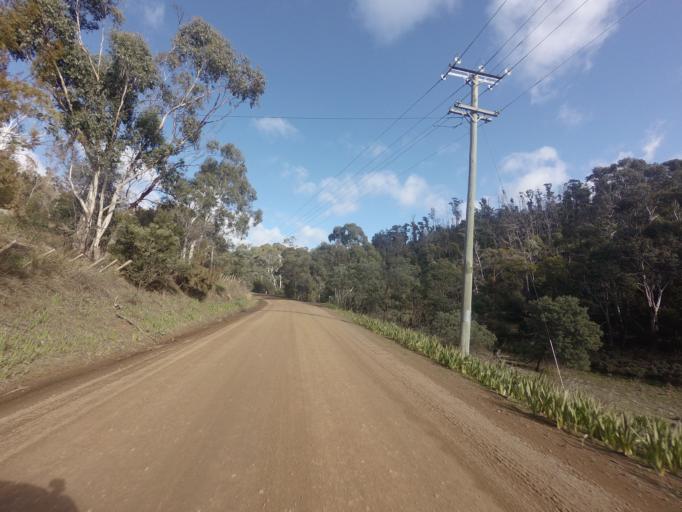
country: AU
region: Tasmania
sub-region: Derwent Valley
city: New Norfolk
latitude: -42.8111
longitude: 147.1313
